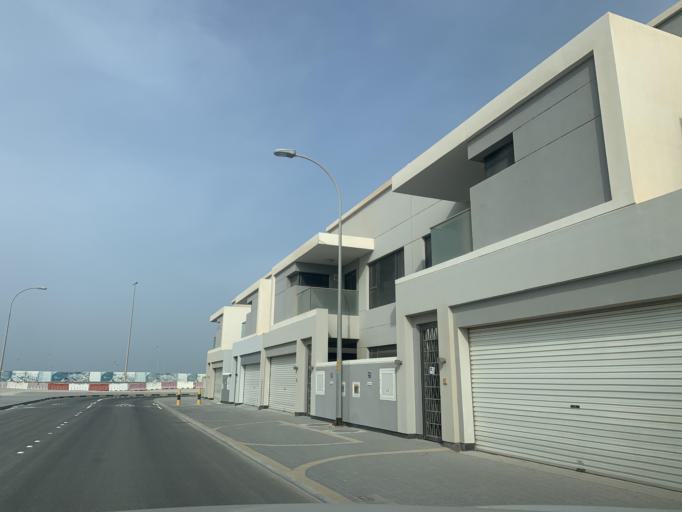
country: BH
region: Muharraq
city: Al Muharraq
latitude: 26.3195
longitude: 50.6293
